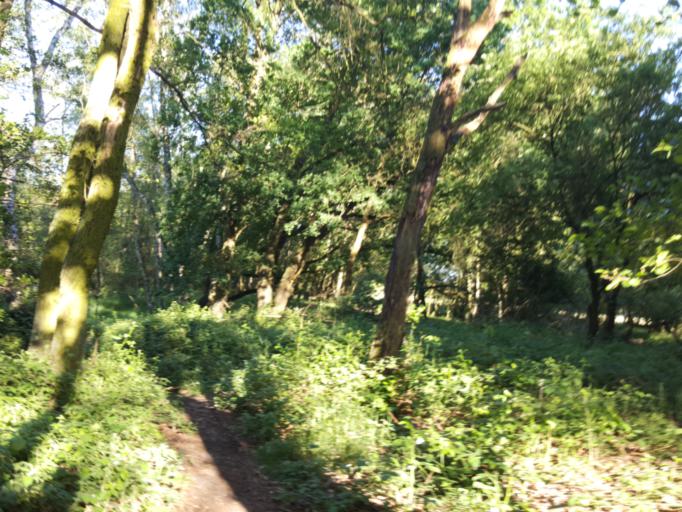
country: DE
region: Schleswig-Holstein
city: Oststeinbek
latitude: 53.5184
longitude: 10.1413
